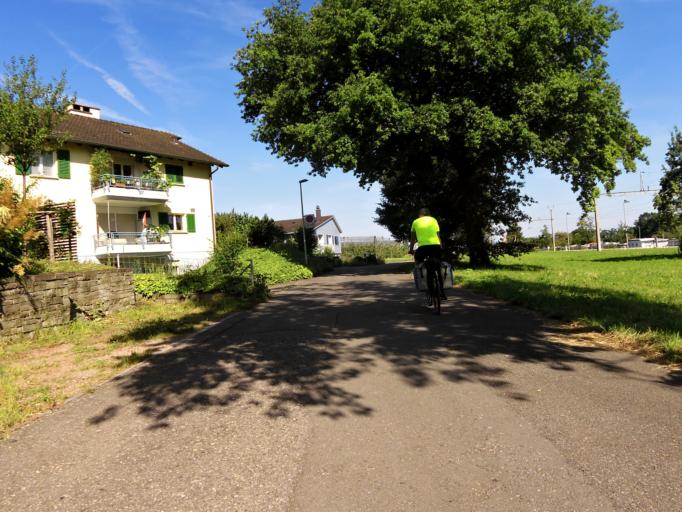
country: CH
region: Thurgau
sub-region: Kreuzlingen District
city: Altnau
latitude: 47.6213
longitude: 9.2655
